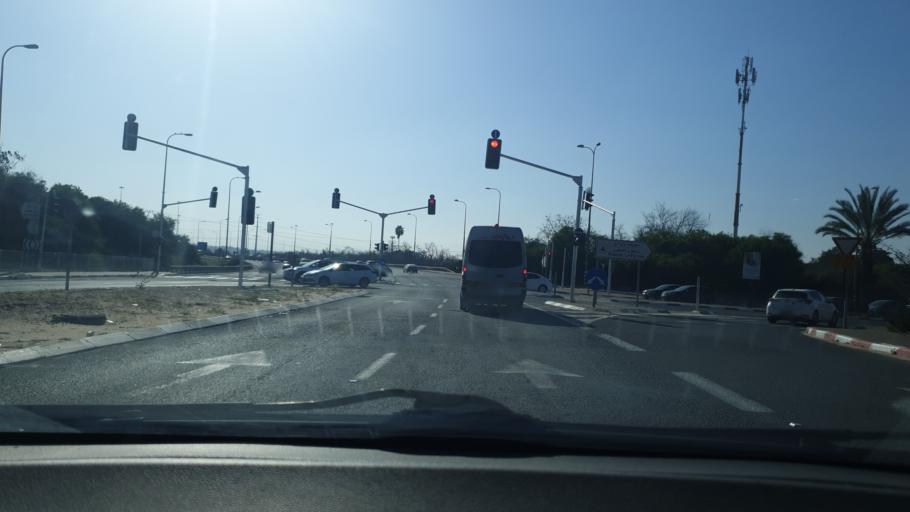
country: IL
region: Central District
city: Ness Ziona
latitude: 31.9440
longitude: 34.8214
